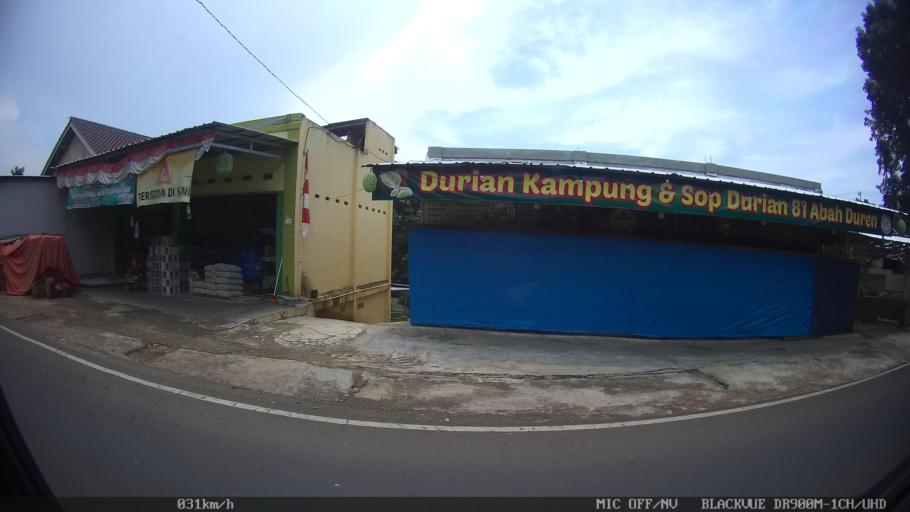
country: ID
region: Lampung
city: Bandarlampung
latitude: -5.4187
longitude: 105.2326
